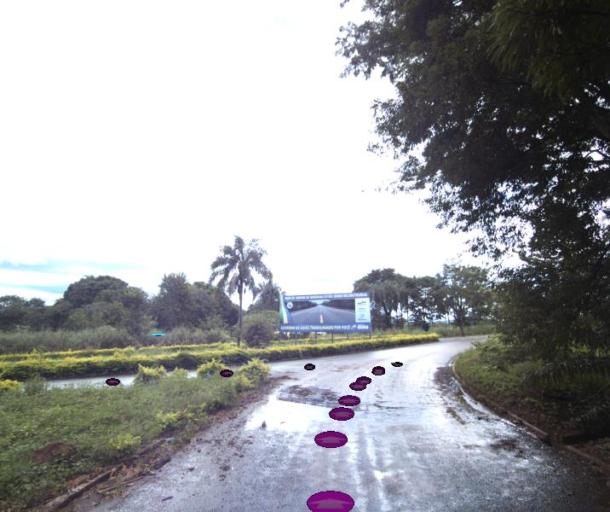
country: BR
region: Goias
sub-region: Pirenopolis
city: Pirenopolis
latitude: -16.0481
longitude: -49.0741
